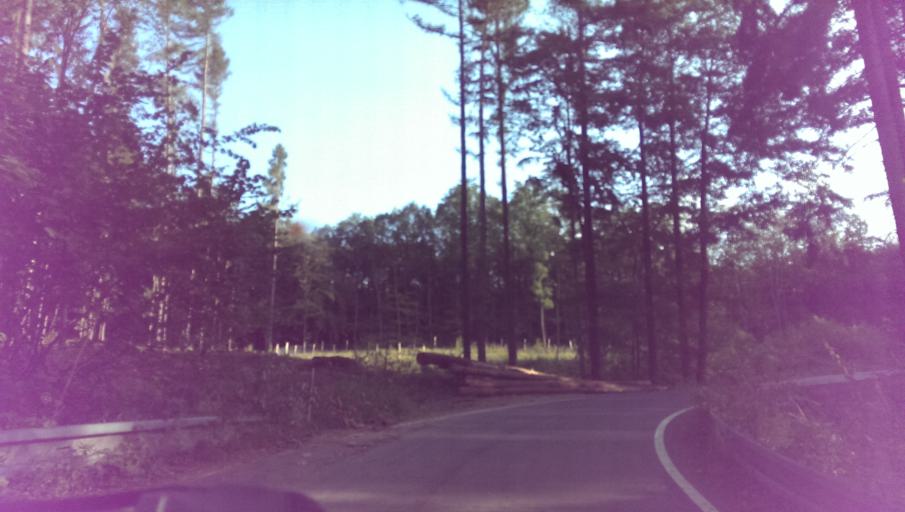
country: CZ
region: Zlin
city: Korycany
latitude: 49.0914
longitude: 17.2069
